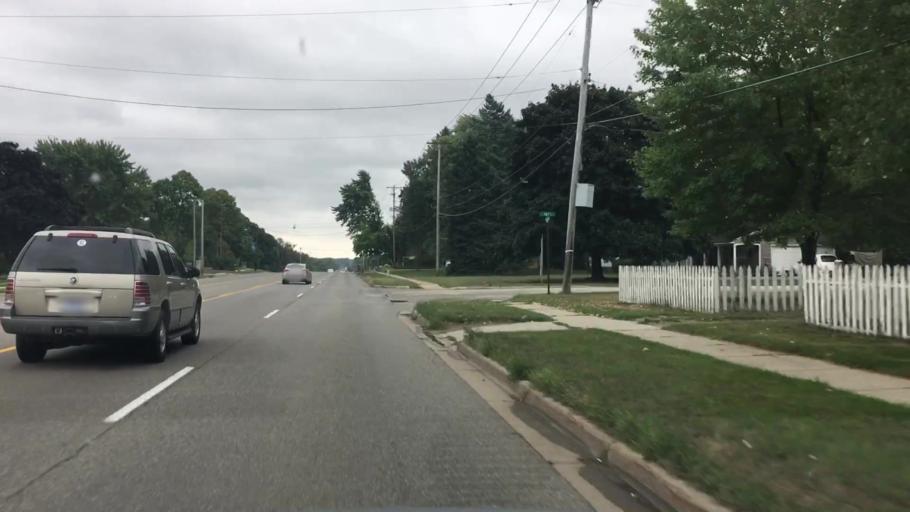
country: US
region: Michigan
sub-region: Ottawa County
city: Jenison
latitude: 42.9070
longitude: -85.8191
